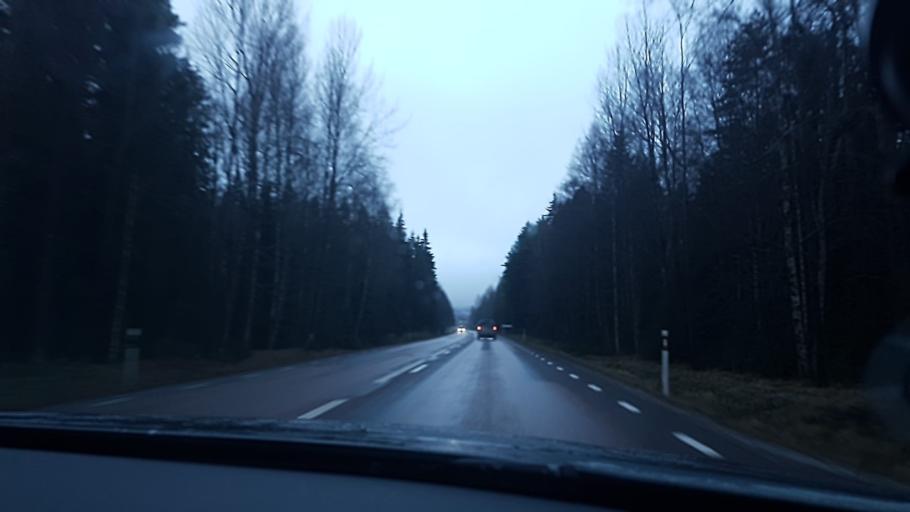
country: SE
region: Vaermland
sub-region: Kristinehamns Kommun
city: Kristinehamn
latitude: 59.3320
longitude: 14.1194
